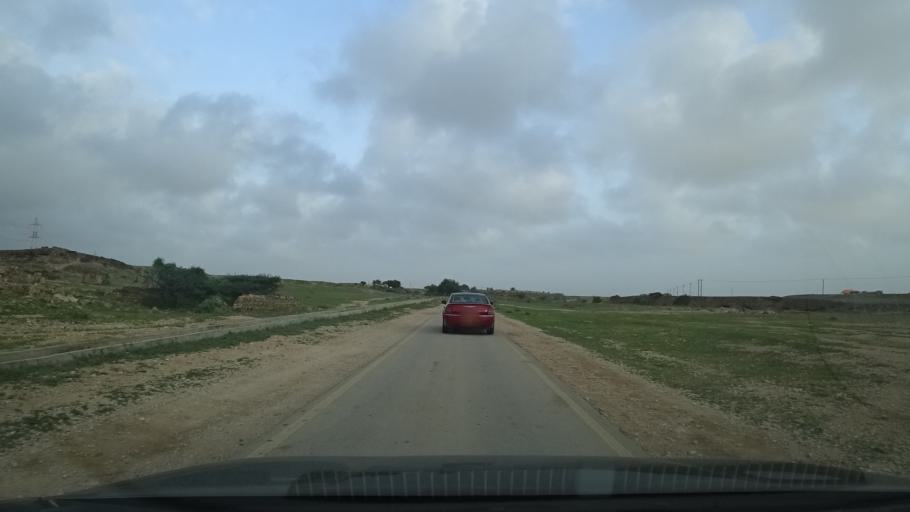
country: OM
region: Zufar
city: Salalah
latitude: 17.1041
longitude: 54.2316
